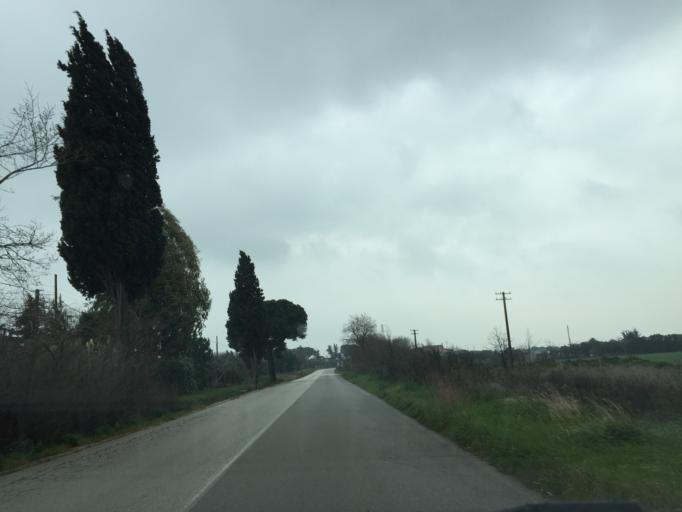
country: IT
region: Apulia
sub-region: Provincia di Foggia
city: Foggia
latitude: 41.4142
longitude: 15.4554
